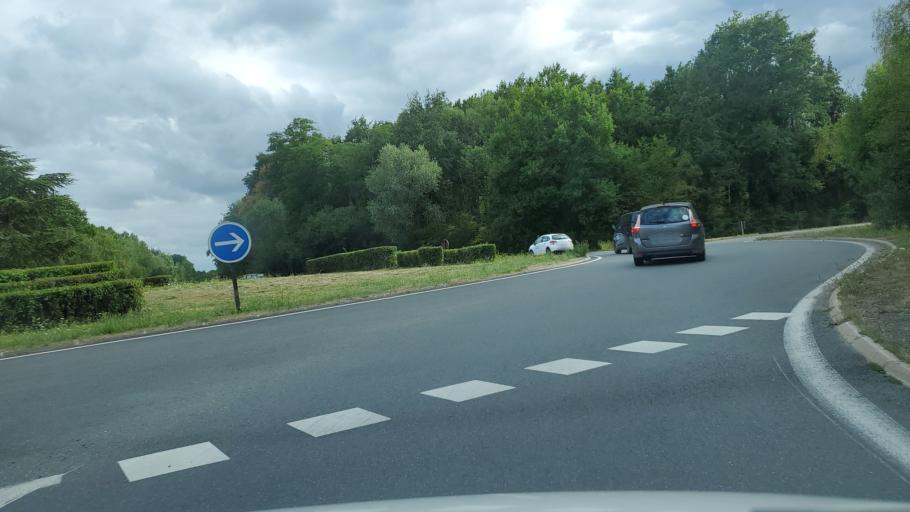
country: FR
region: Ile-de-France
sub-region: Departement de Seine-et-Marne
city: Villeneuve-le-Comte
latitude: 48.8155
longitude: 2.8418
